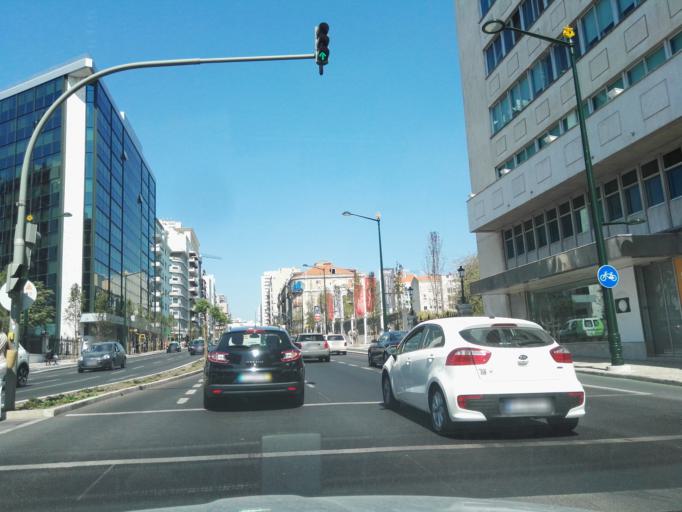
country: PT
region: Lisbon
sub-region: Lisbon
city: Lisbon
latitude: 38.7280
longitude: -9.1483
